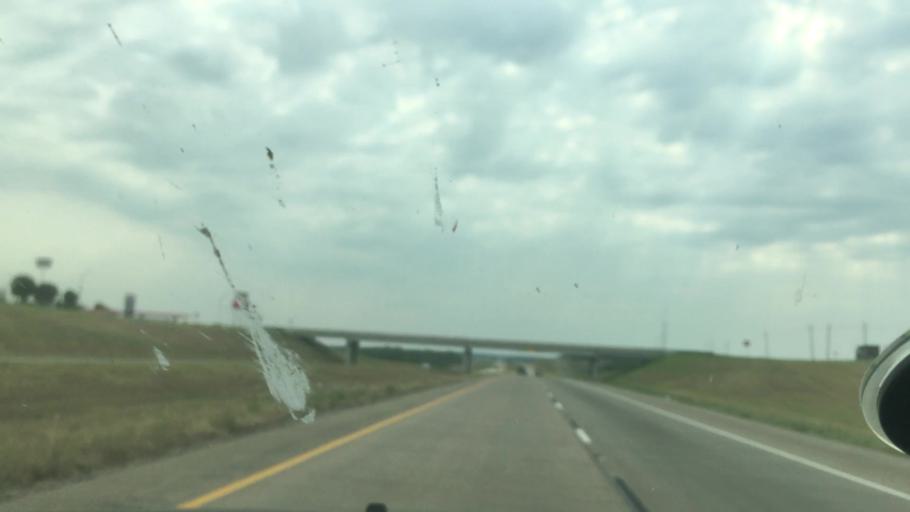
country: US
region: Texas
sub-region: Grayson County
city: Denison
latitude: 33.7939
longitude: -96.5582
